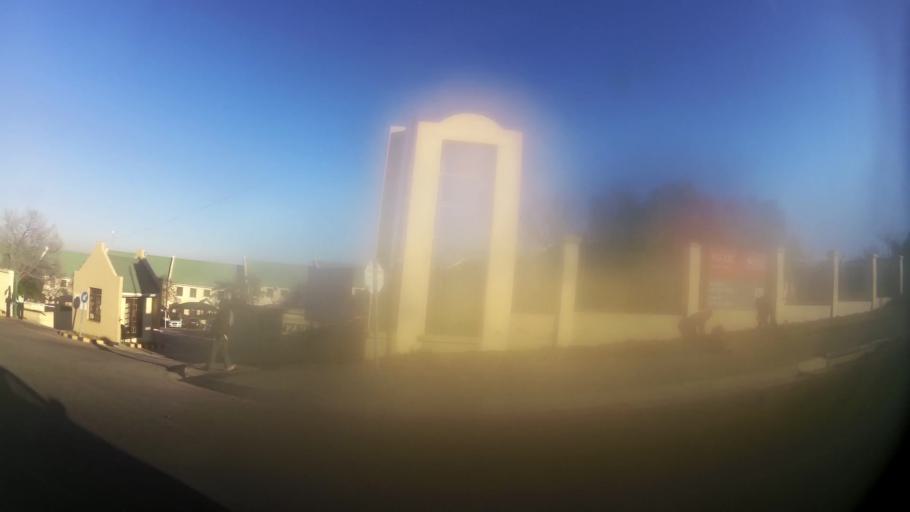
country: ZA
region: Gauteng
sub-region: City of Johannesburg Metropolitan Municipality
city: Midrand
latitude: -26.0038
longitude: 28.1238
